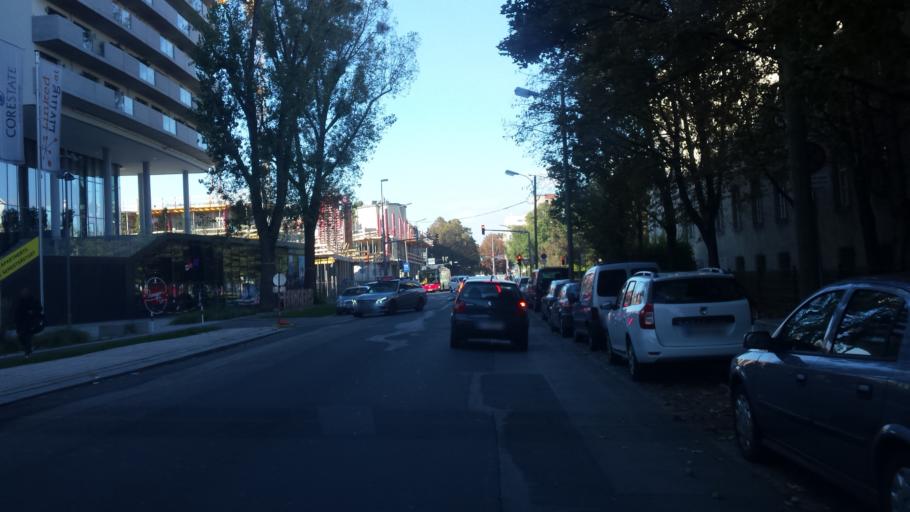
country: AT
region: Vienna
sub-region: Wien Stadt
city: Vienna
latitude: 48.2166
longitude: 16.4120
